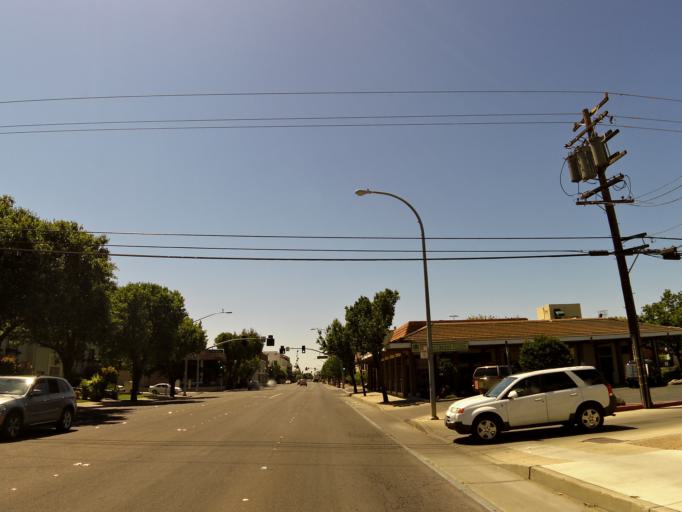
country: US
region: California
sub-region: Merced County
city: Merced
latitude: 37.3047
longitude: -120.4834
